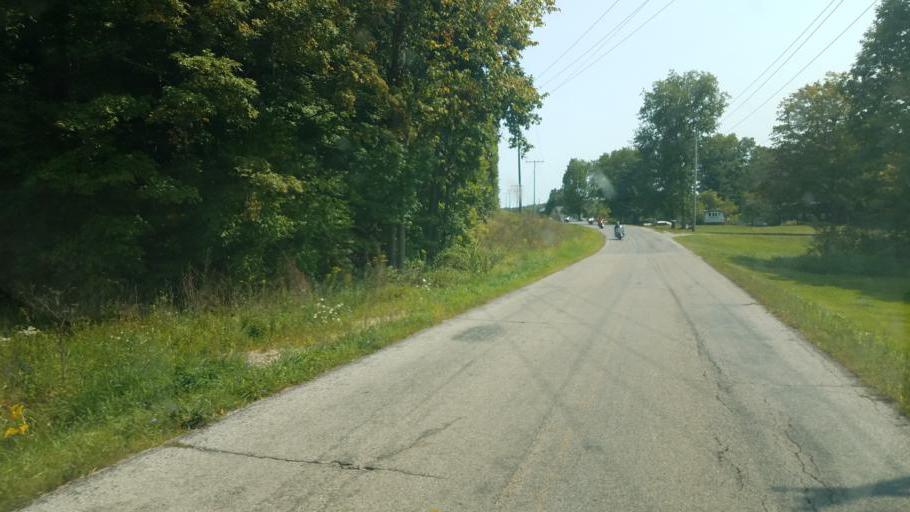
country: US
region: Ohio
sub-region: Sandusky County
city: Bellville
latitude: 40.5610
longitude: -82.5191
